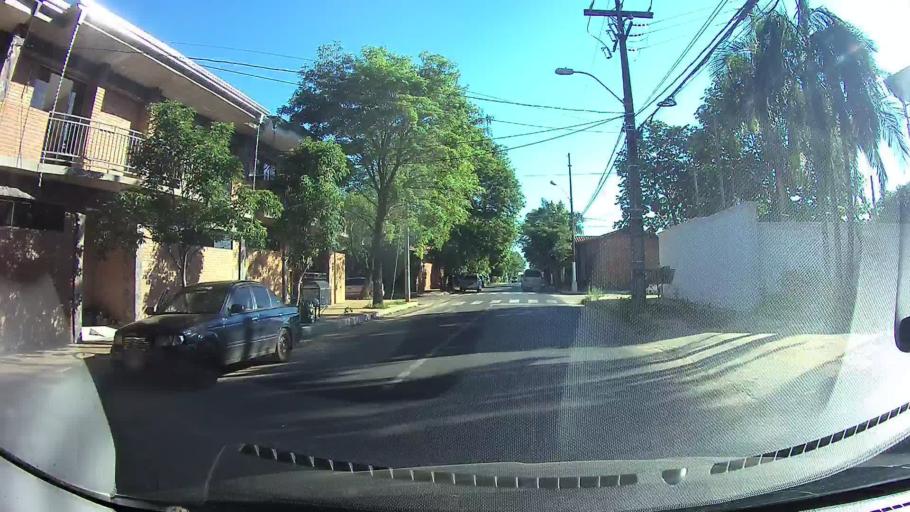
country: PY
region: Central
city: Fernando de la Mora
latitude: -25.2943
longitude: -57.5578
